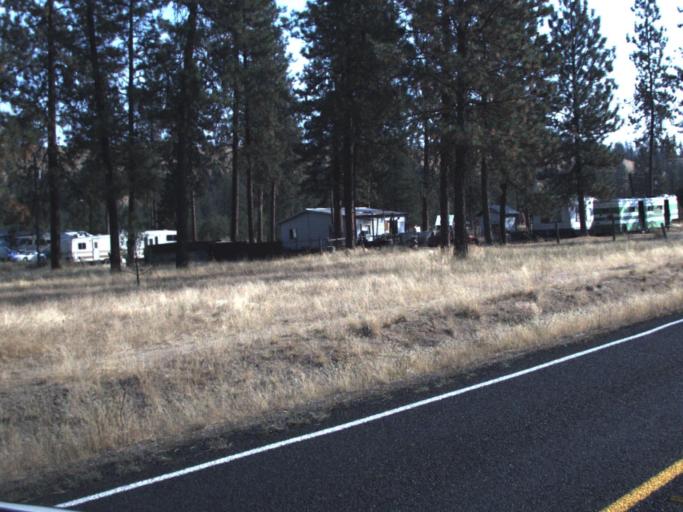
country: US
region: Washington
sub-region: Spokane County
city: Fairchild Air Force Base
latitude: 47.8392
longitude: -117.8103
